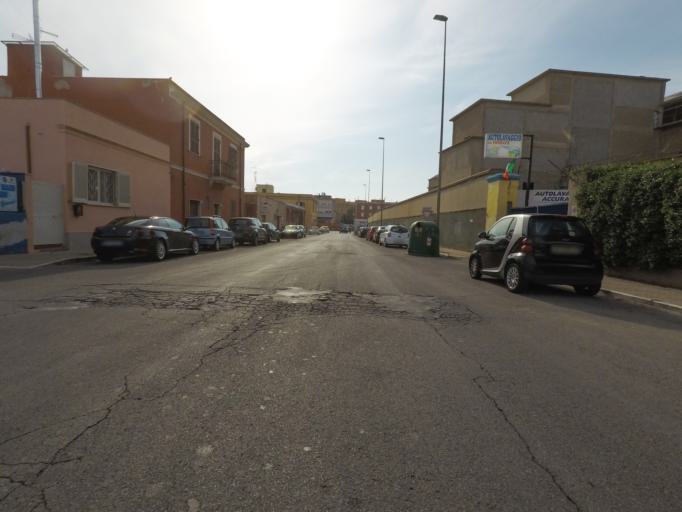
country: IT
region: Latium
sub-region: Citta metropolitana di Roma Capitale
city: Civitavecchia
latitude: 42.0966
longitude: 11.7952
